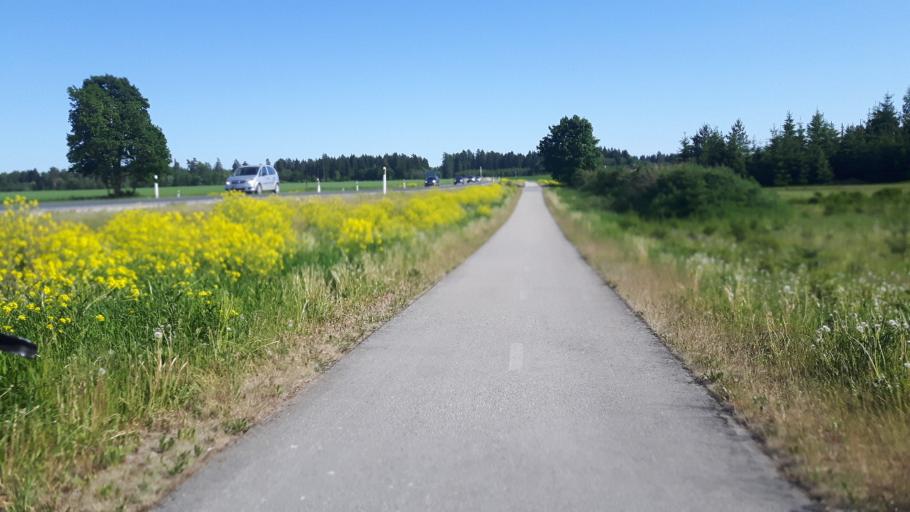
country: EE
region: Raplamaa
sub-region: Kehtna vald
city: Kehtna
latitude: 58.9670
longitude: 24.8550
